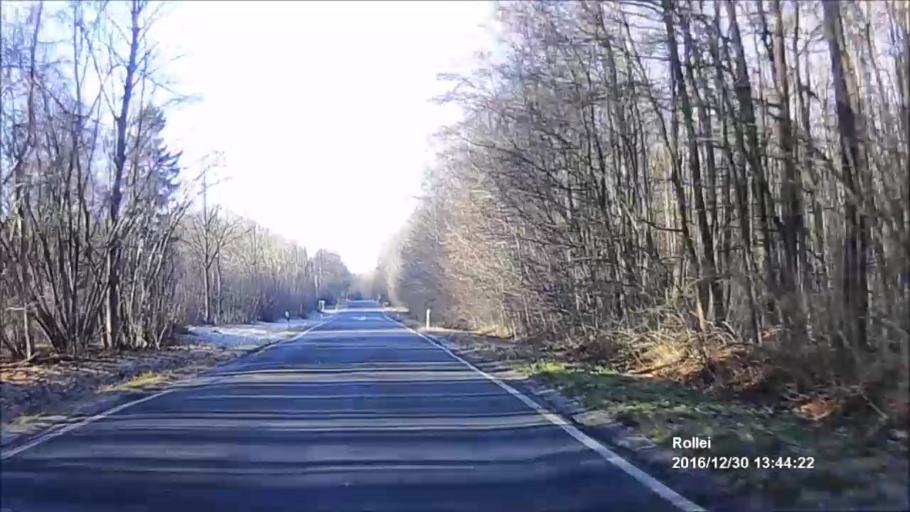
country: DE
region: Thuringia
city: Rockhausen
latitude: 50.9193
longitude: 11.0828
